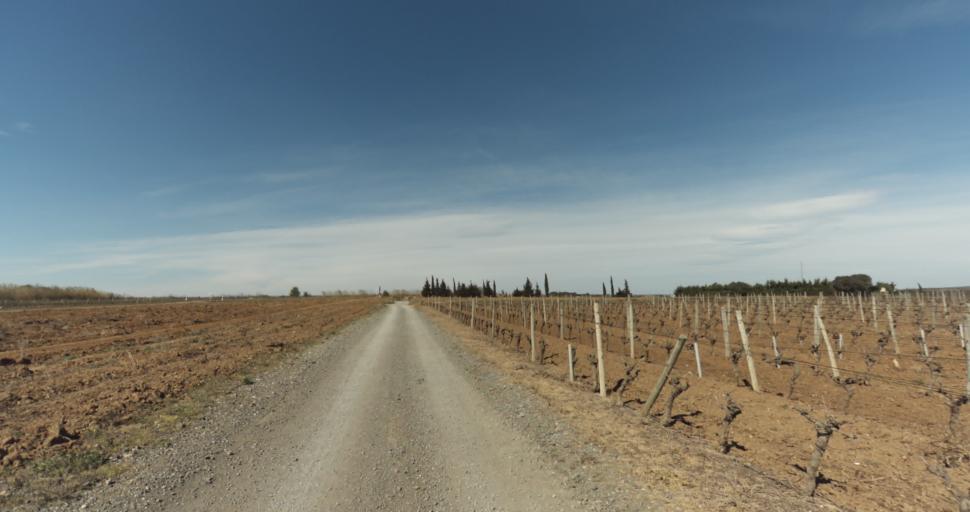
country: FR
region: Languedoc-Roussillon
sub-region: Departement de l'Herault
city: Marseillan
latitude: 43.3767
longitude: 3.5360
